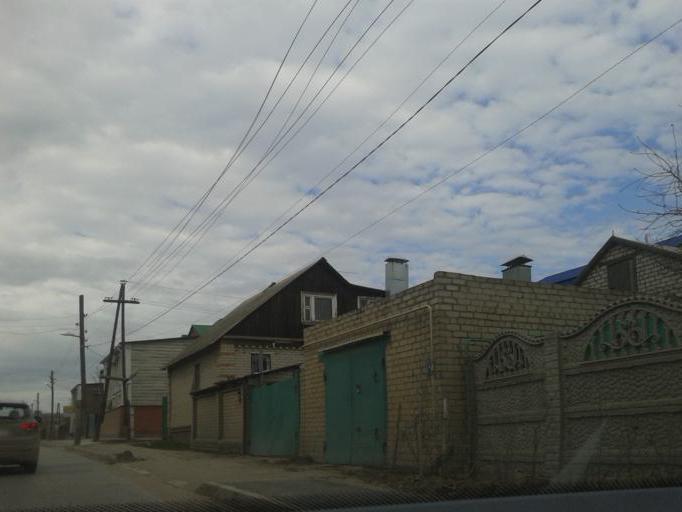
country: RU
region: Volgograd
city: Volgograd
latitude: 48.7002
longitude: 44.4491
